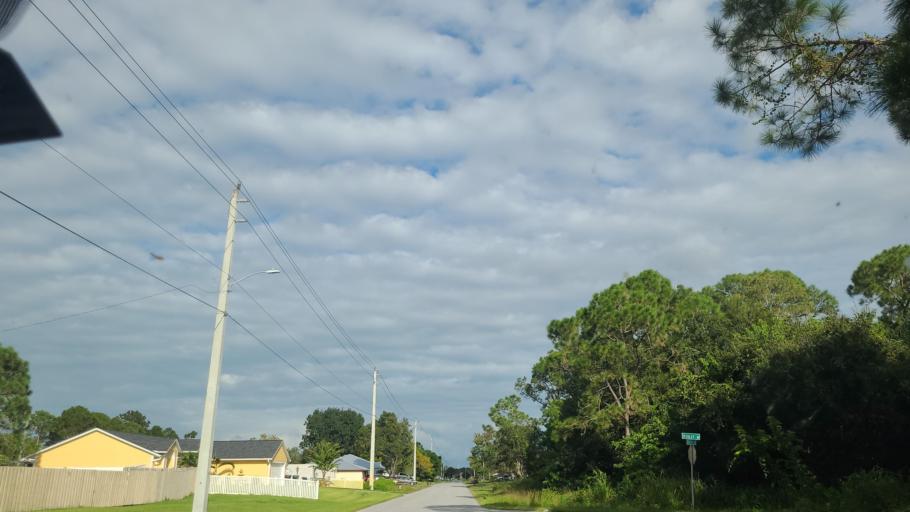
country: US
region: Florida
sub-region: Brevard County
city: Palm Bay
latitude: 27.9836
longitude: -80.6459
